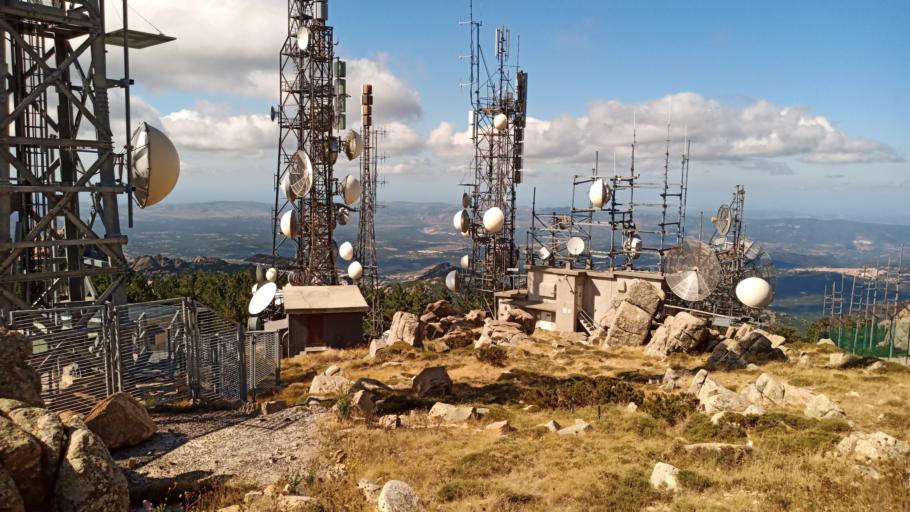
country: IT
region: Sardinia
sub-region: Provincia di Olbia-Tempio
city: Berchidda
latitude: 40.8527
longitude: 9.1754
